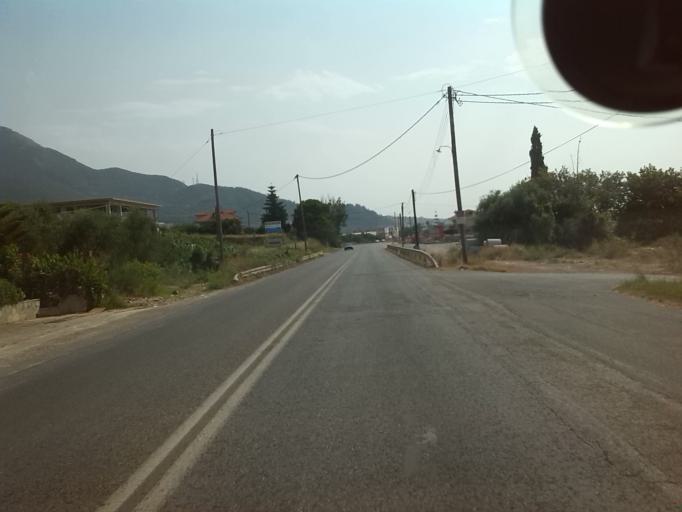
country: GR
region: Peloponnese
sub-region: Nomos Messinias
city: Kyparissia
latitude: 37.2711
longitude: 21.6957
